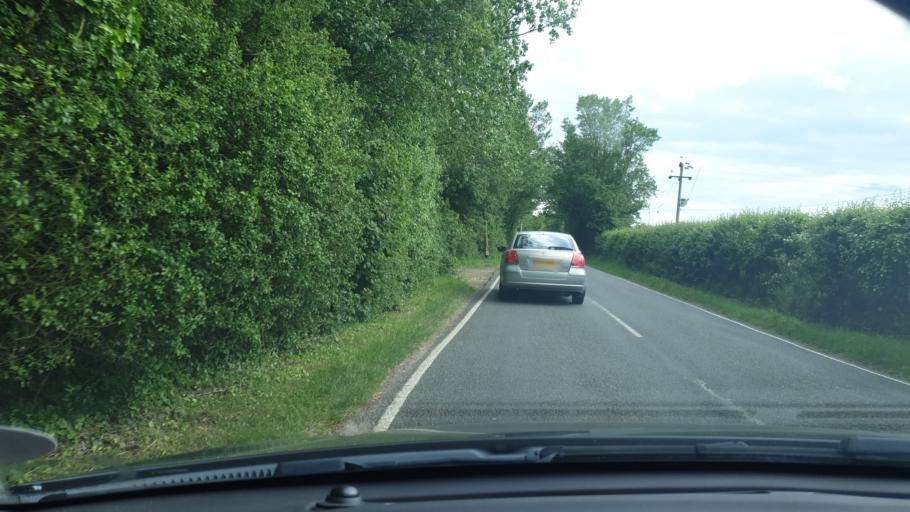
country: GB
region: England
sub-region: Essex
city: Great Bentley
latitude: 51.8625
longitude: 1.1003
